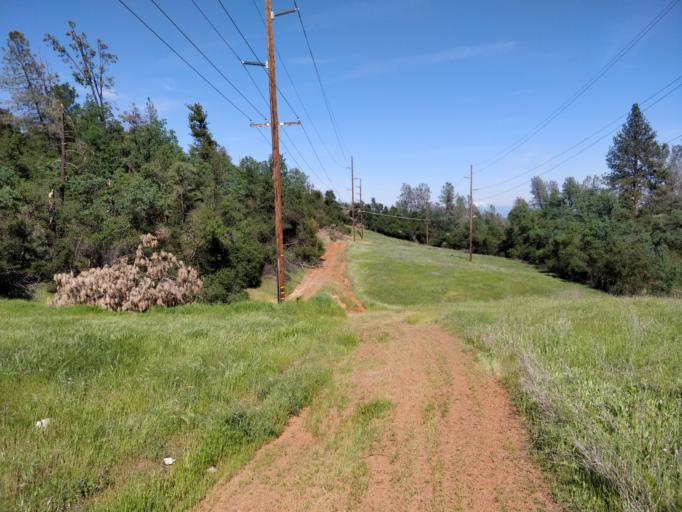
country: US
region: California
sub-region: Shasta County
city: Central Valley (historical)
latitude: 40.6684
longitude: -122.3715
